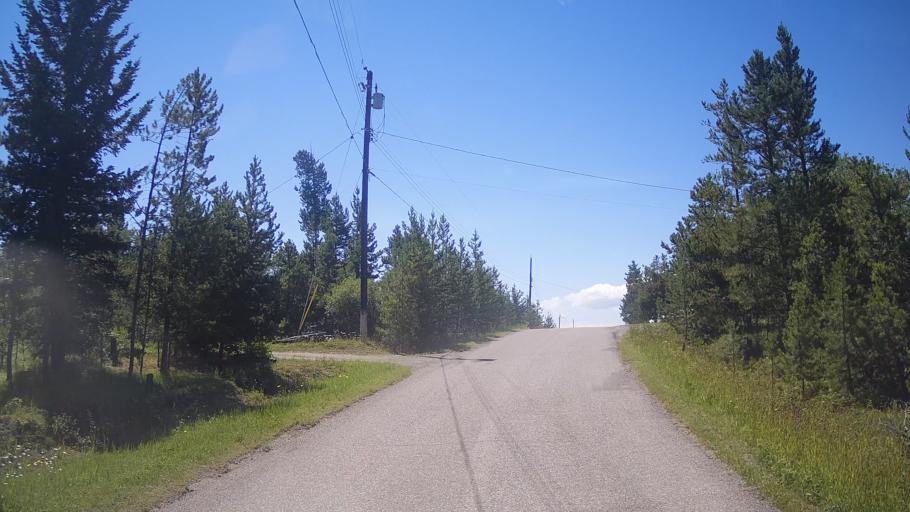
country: CA
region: British Columbia
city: Cache Creek
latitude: 51.3149
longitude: -121.3939
